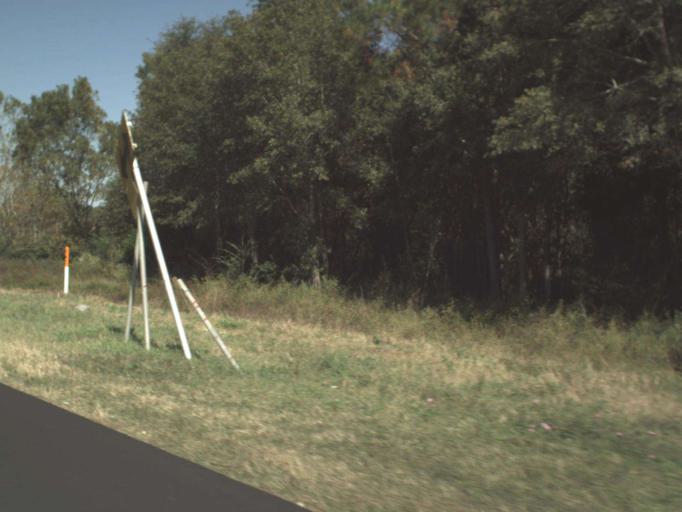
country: US
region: Florida
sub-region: Walton County
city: DeFuniak Springs
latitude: 30.8314
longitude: -86.2319
